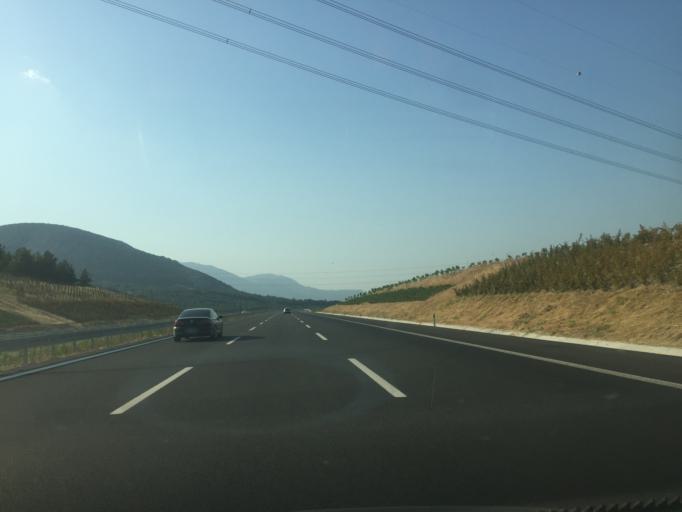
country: TR
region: Manisa
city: Kirkagac
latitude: 39.0599
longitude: 27.7245
